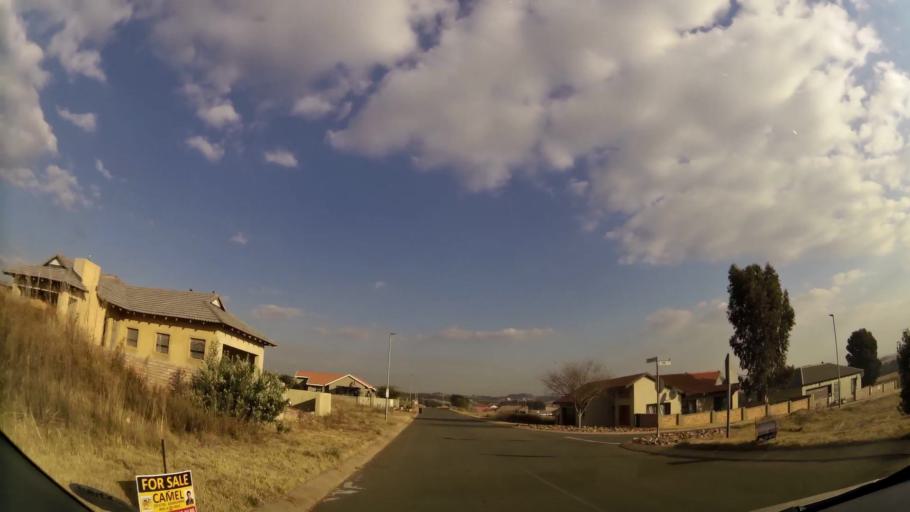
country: ZA
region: Gauteng
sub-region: West Rand District Municipality
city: Krugersdorp
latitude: -26.1001
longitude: 27.7301
